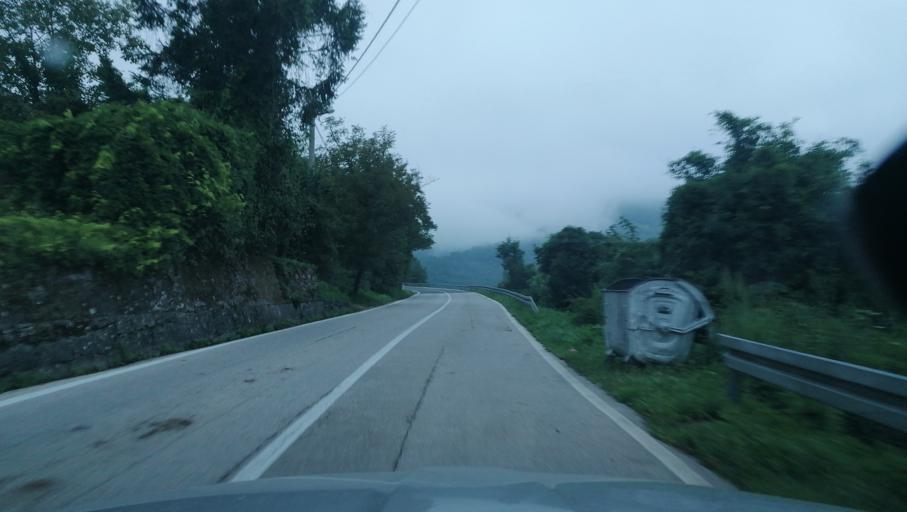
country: BA
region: Federation of Bosnia and Herzegovina
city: Jablanica
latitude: 43.7090
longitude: 17.7173
